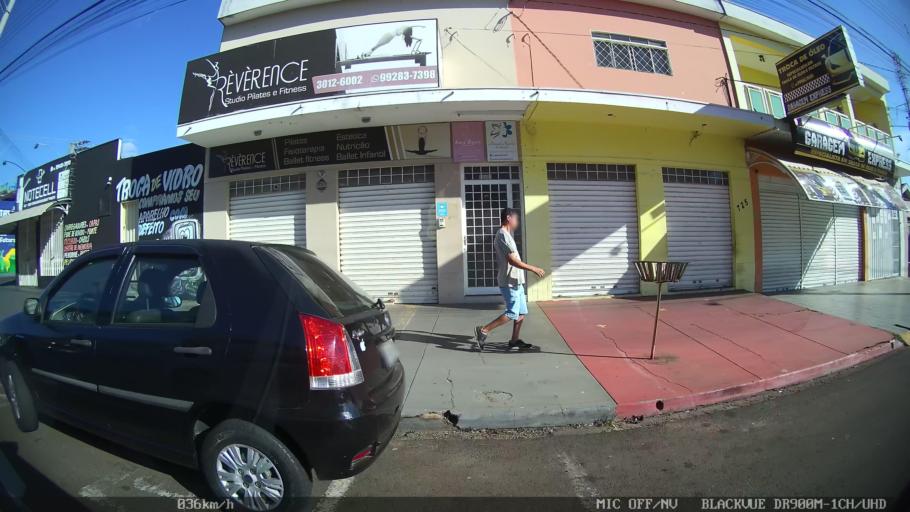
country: BR
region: Sao Paulo
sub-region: Franca
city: Franca
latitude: -20.5292
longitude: -47.4274
